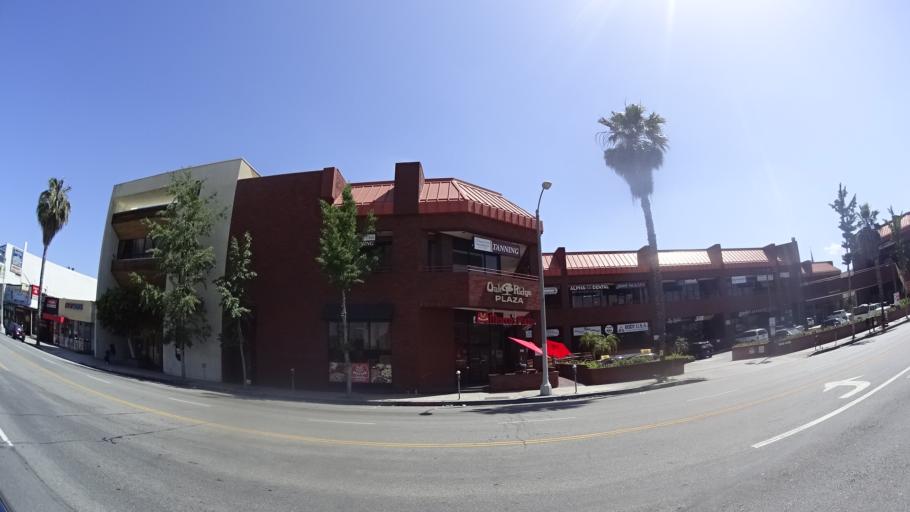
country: US
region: California
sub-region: Los Angeles County
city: Sherman Oaks
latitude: 34.1504
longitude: -118.4449
